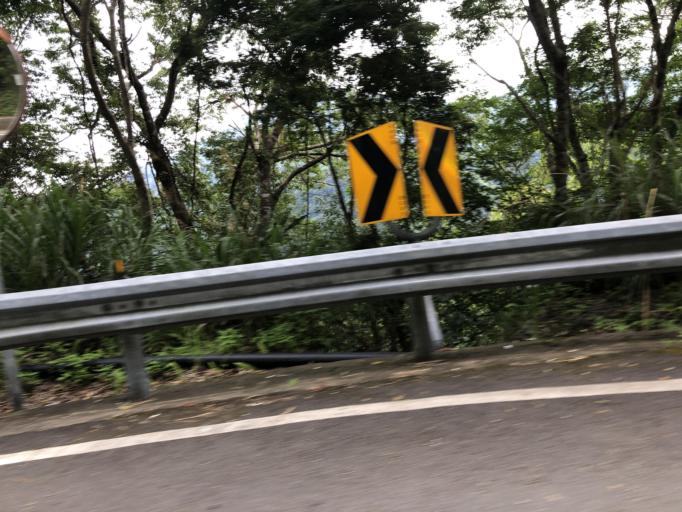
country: TW
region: Taiwan
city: Daxi
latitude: 24.6989
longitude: 121.3655
